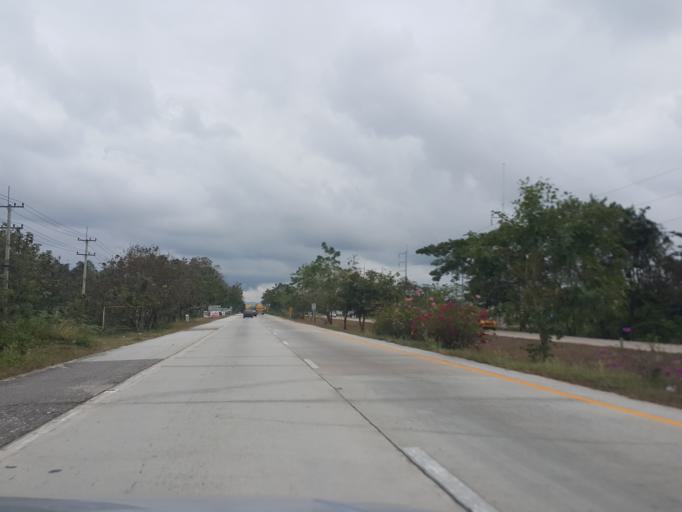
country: TH
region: Lampang
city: Hang Chat
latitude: 18.2991
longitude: 99.4104
